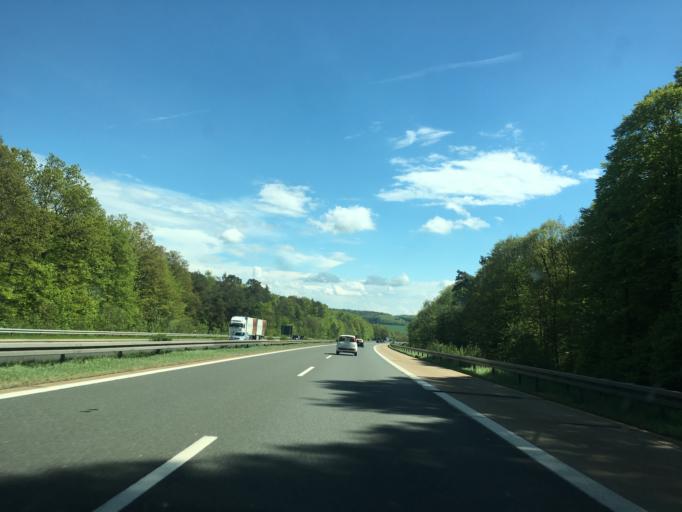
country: DE
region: Bavaria
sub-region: Regierungsbezirk Unterfranken
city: Oberthulba
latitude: 50.2038
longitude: 9.9349
